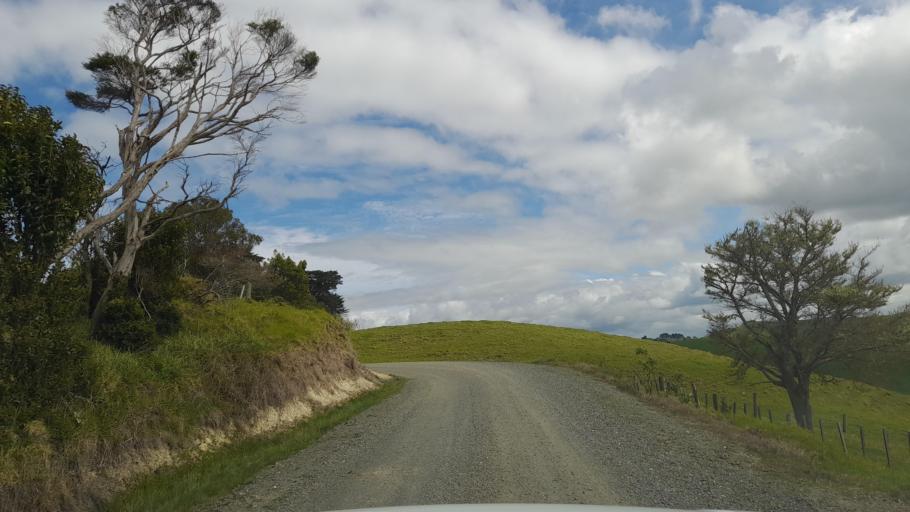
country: NZ
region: Auckland
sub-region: Auckland
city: Wellsford
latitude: -36.2145
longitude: 174.3227
